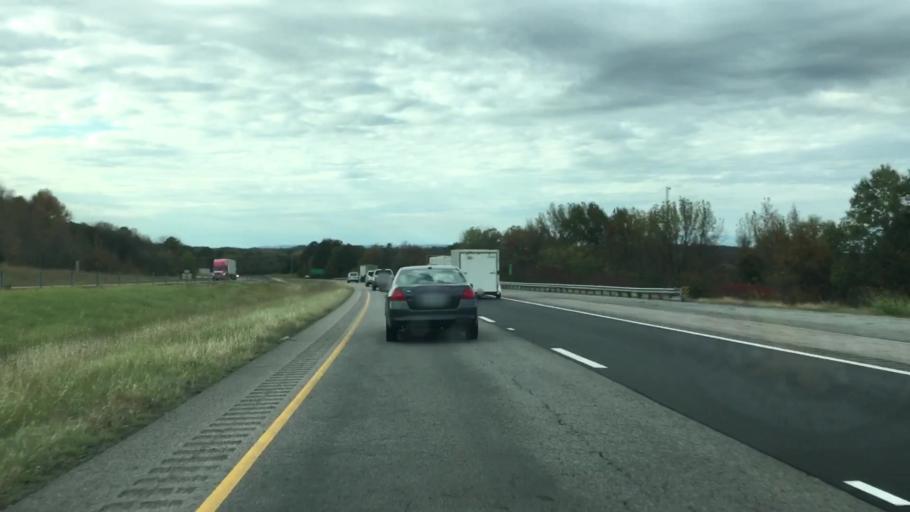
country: US
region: Arkansas
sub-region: Conway County
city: Morrilton
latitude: 35.1728
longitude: -92.6998
